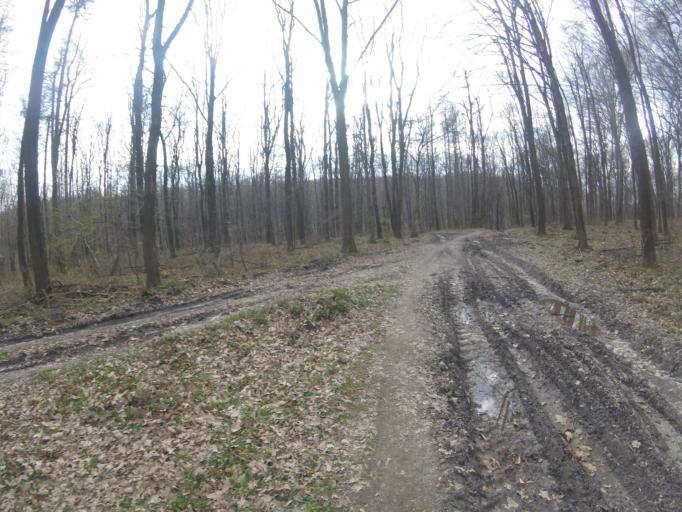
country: HU
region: Fejer
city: Szarliget
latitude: 47.4858
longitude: 18.4203
